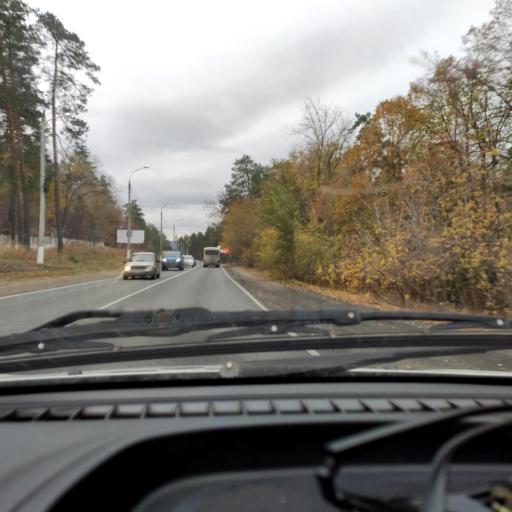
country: RU
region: Samara
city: Tol'yatti
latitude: 53.4856
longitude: 49.3145
